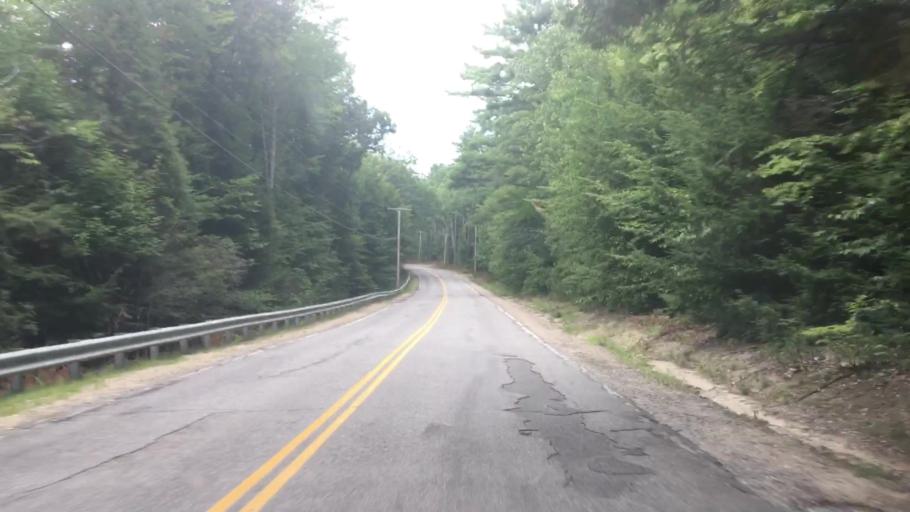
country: US
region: Maine
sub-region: Oxford County
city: Oxford
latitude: 44.0285
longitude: -70.5310
